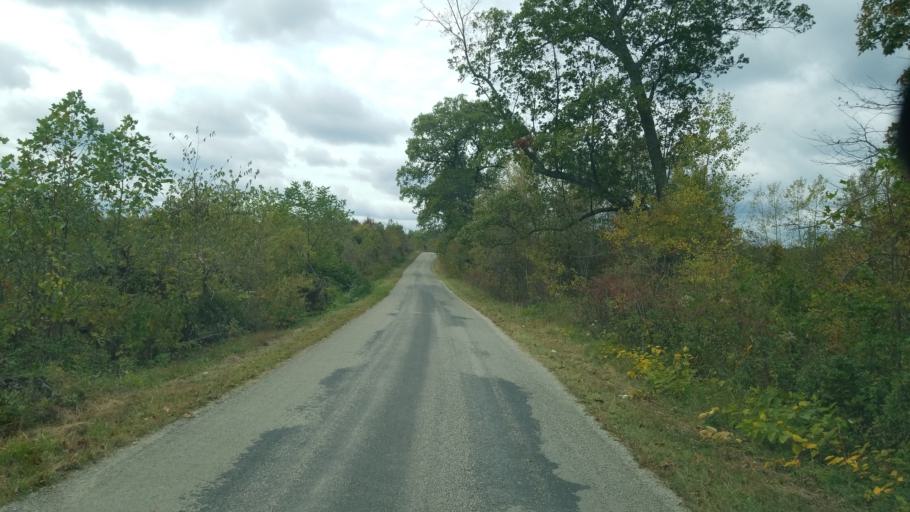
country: US
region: Ohio
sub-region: Jackson County
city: Wellston
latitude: 39.1611
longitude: -82.5863
